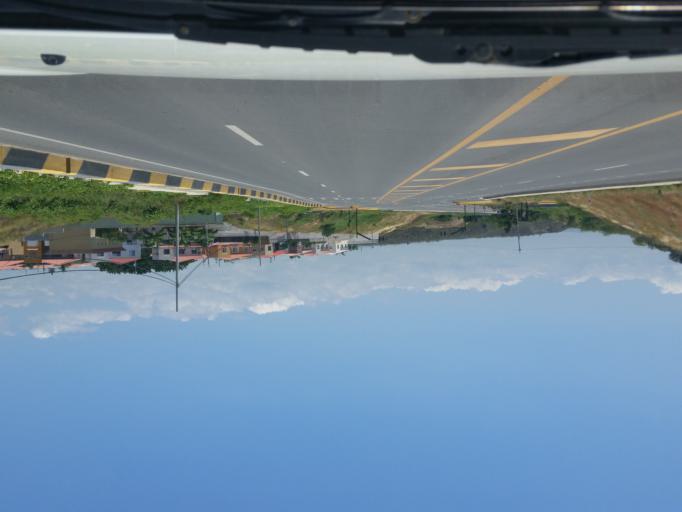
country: EC
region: Manabi
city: Manta
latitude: -0.9606
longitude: -80.7559
